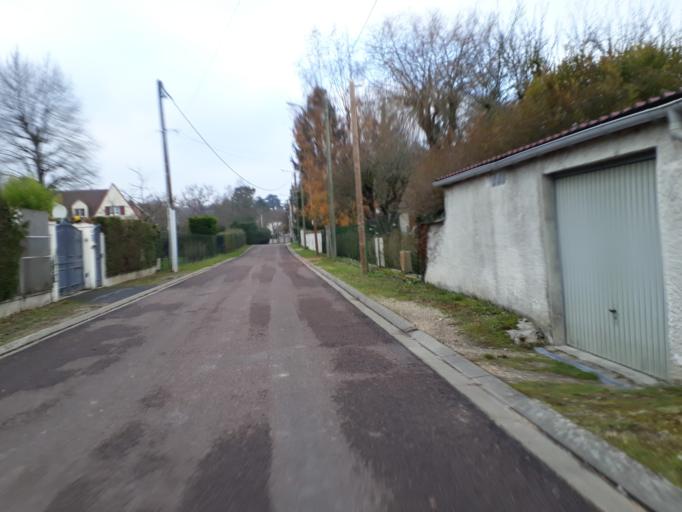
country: FR
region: Ile-de-France
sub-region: Departement de Seine-et-Marne
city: Chartrettes
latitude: 48.4794
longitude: 2.6758
